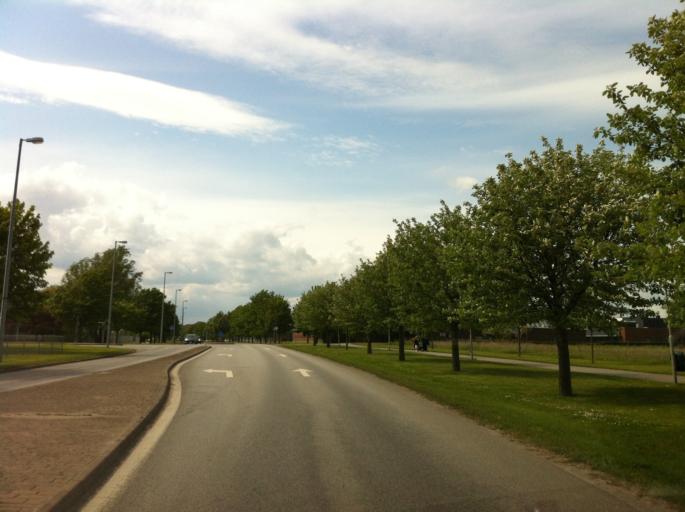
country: SE
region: Skane
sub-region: Landskrona
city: Landskrona
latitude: 55.8809
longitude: 12.8535
